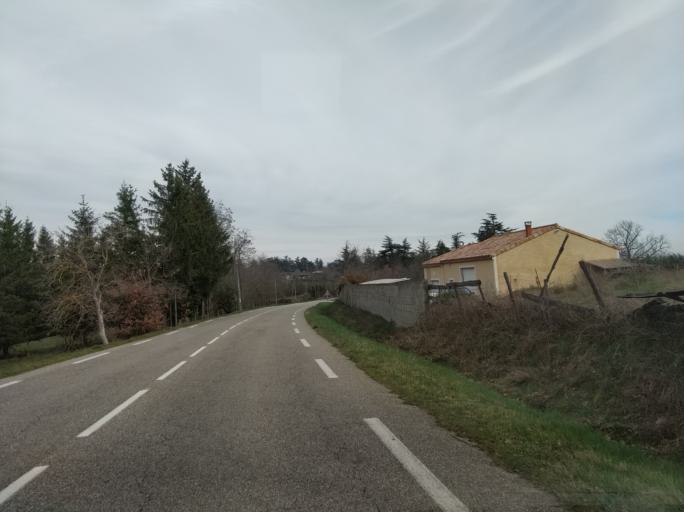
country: FR
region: Rhone-Alpes
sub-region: Departement de l'Ardeche
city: Roiffieux
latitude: 45.2158
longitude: 4.6608
